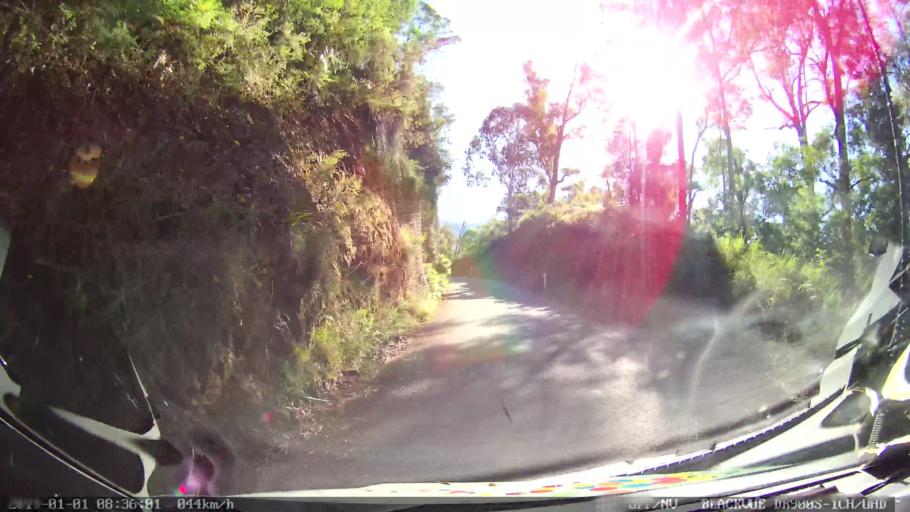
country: AU
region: New South Wales
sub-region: Snowy River
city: Jindabyne
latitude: -36.3461
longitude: 148.1938
